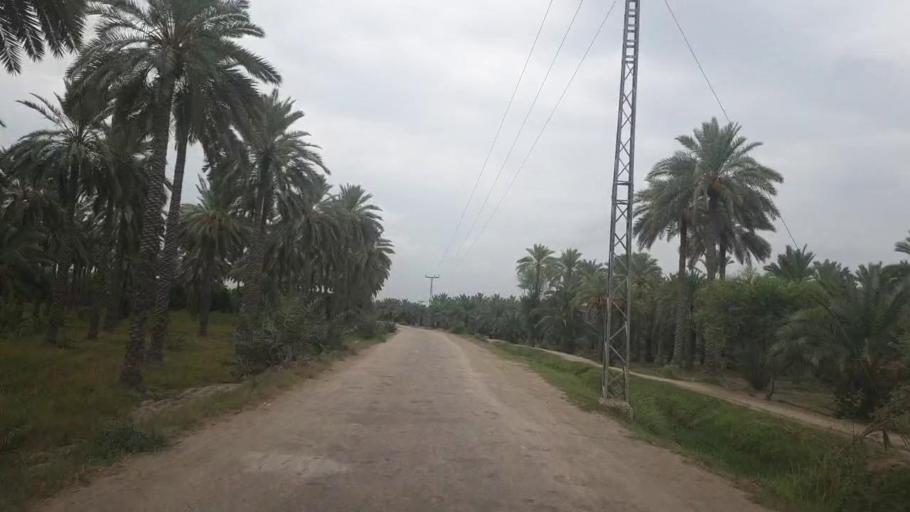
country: PK
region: Sindh
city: Khairpur
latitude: 27.5706
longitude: 68.7036
